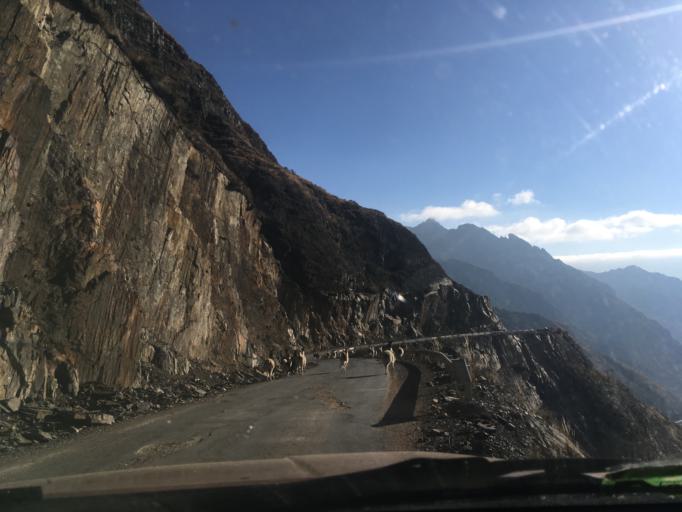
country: BO
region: La Paz
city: Quime
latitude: -17.0103
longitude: -67.2757
